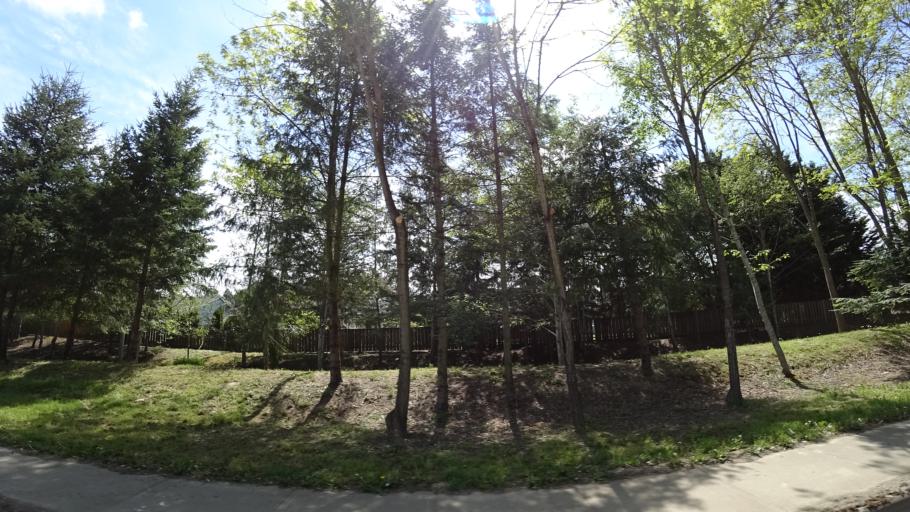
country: US
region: Oregon
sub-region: Washington County
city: Aloha
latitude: 45.4680
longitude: -122.8891
